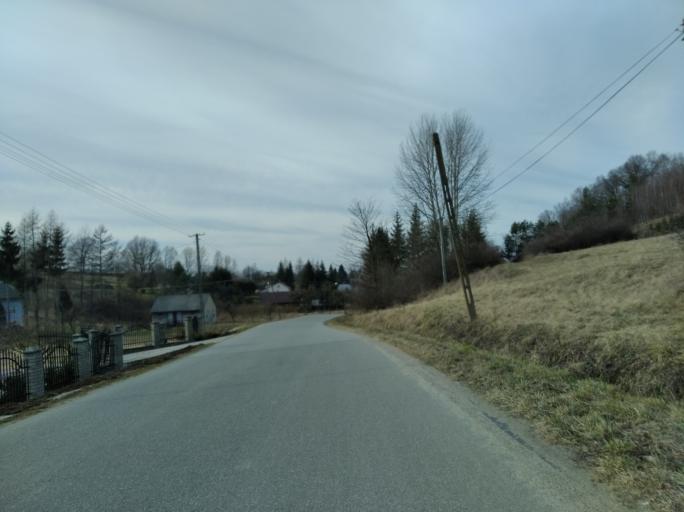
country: PL
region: Subcarpathian Voivodeship
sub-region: Powiat brzozowski
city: Gorki
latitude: 49.6405
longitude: 22.0545
